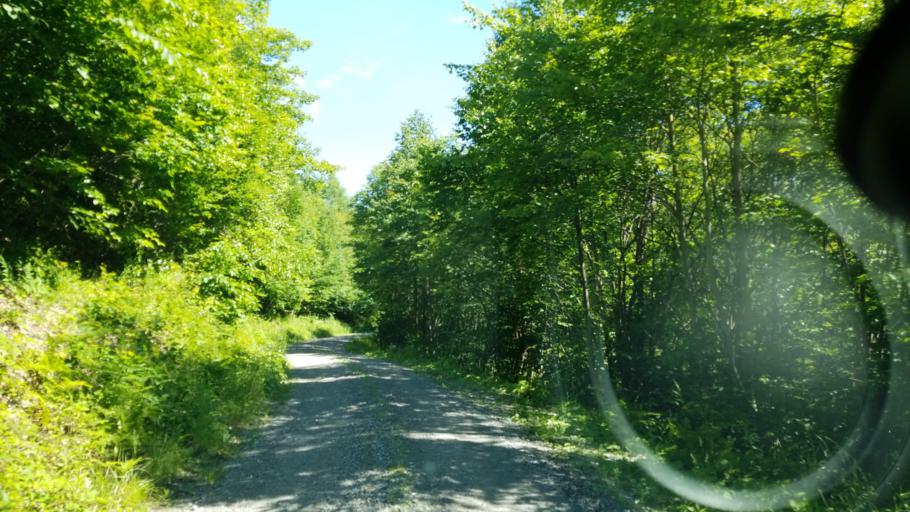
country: US
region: Pennsylvania
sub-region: Clearfield County
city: Clearfield
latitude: 41.2149
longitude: -78.3871
